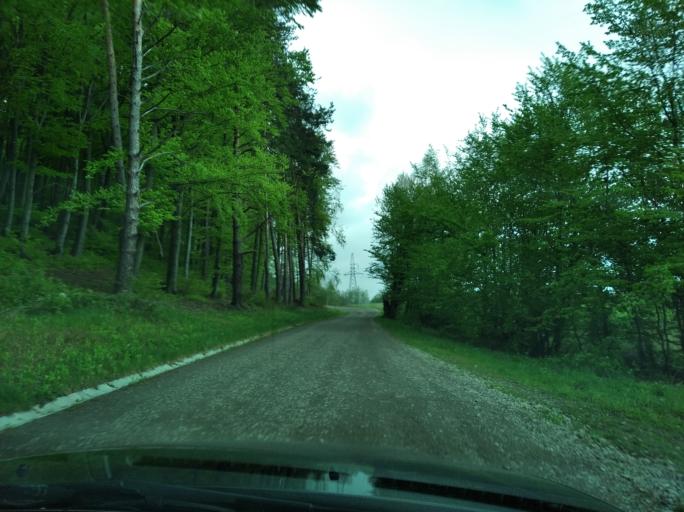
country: PL
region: Subcarpathian Voivodeship
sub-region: Powiat sanocki
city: Sanok
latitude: 49.5663
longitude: 22.2315
